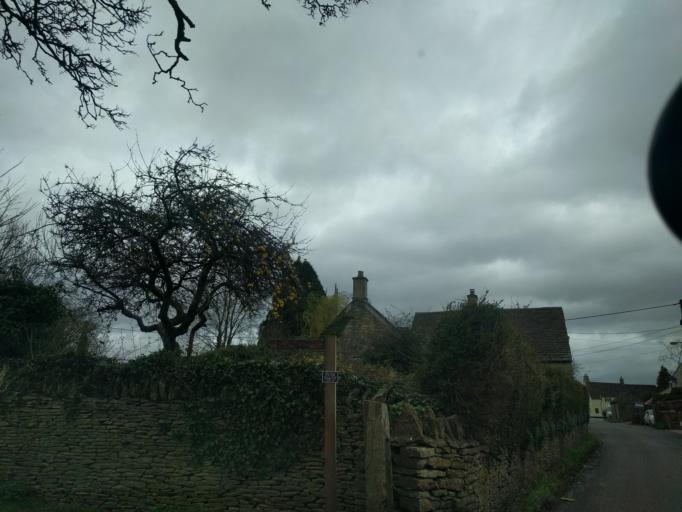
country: GB
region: England
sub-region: Wiltshire
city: Biddestone
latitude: 51.4854
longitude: -2.1939
